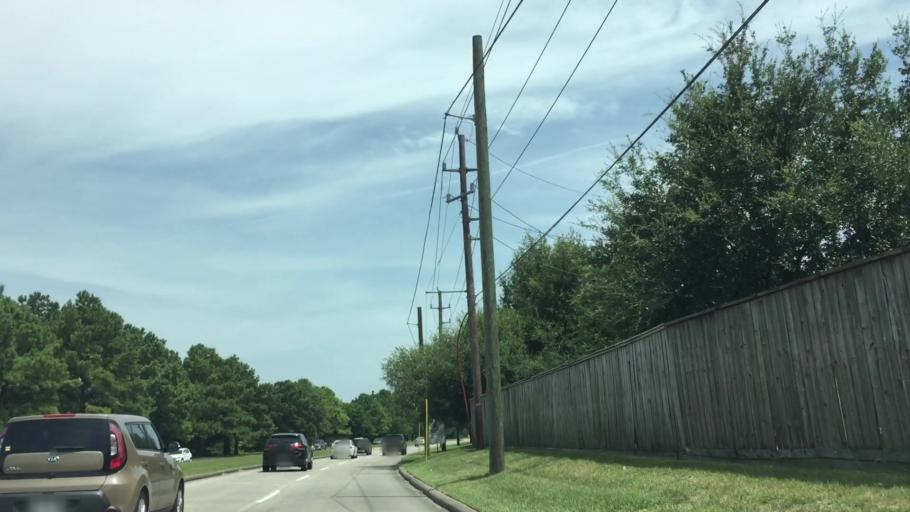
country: US
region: Texas
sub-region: Harris County
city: Jersey Village
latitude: 29.9087
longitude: -95.5640
